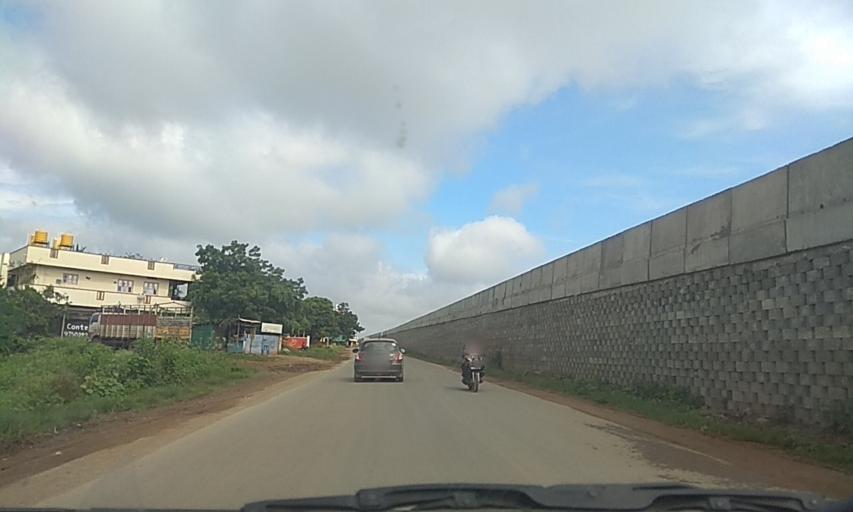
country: IN
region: Karnataka
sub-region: Haveri
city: Shiggaon
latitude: 14.9915
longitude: 75.2167
